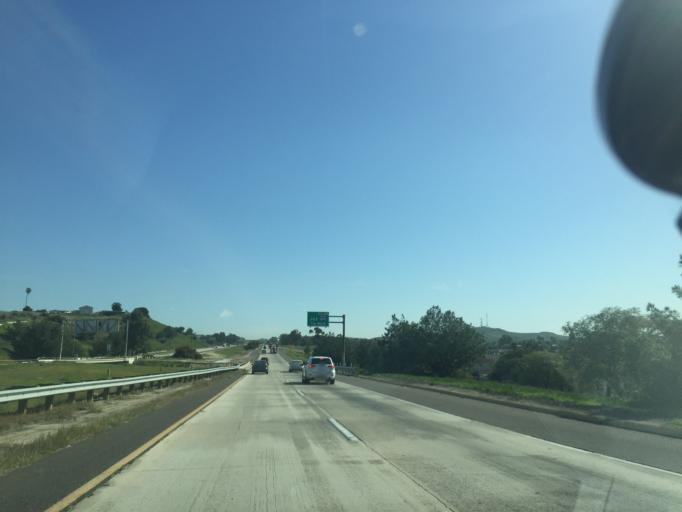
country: US
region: California
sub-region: San Diego County
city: Imperial Beach
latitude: 32.5682
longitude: -117.0549
